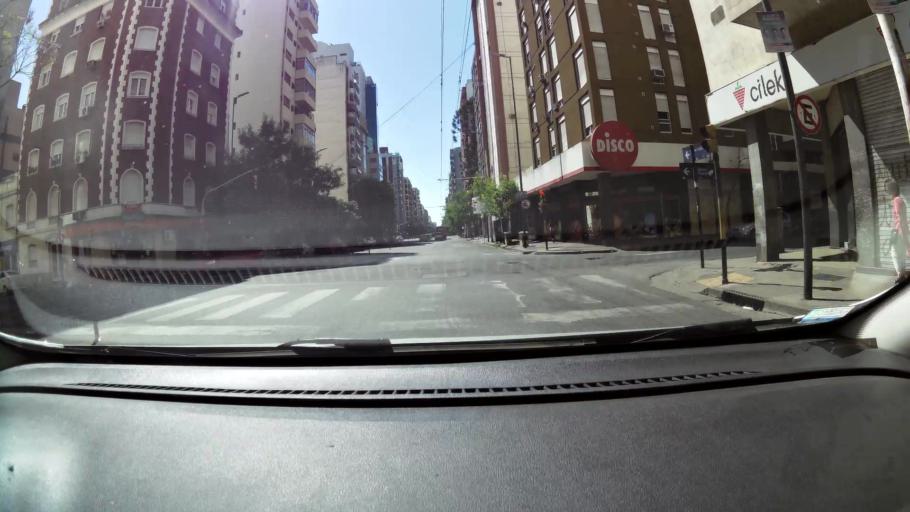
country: AR
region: Cordoba
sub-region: Departamento de Capital
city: Cordoba
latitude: -31.4108
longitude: -64.1927
